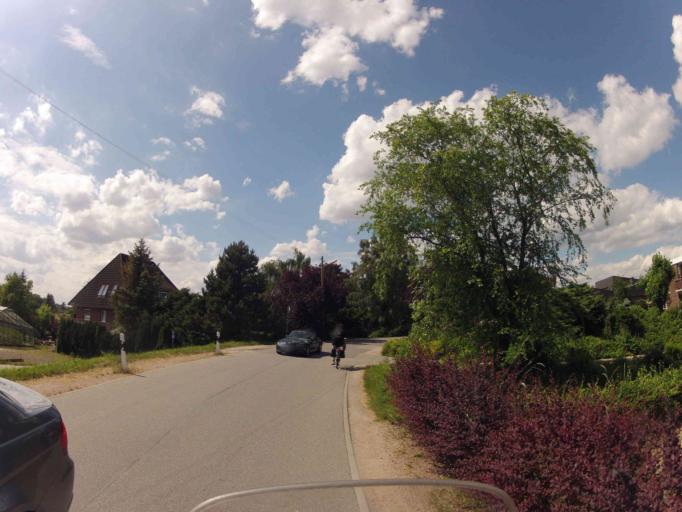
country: DE
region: Hamburg
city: Rothenburgsort
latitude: 53.4946
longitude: 10.0837
